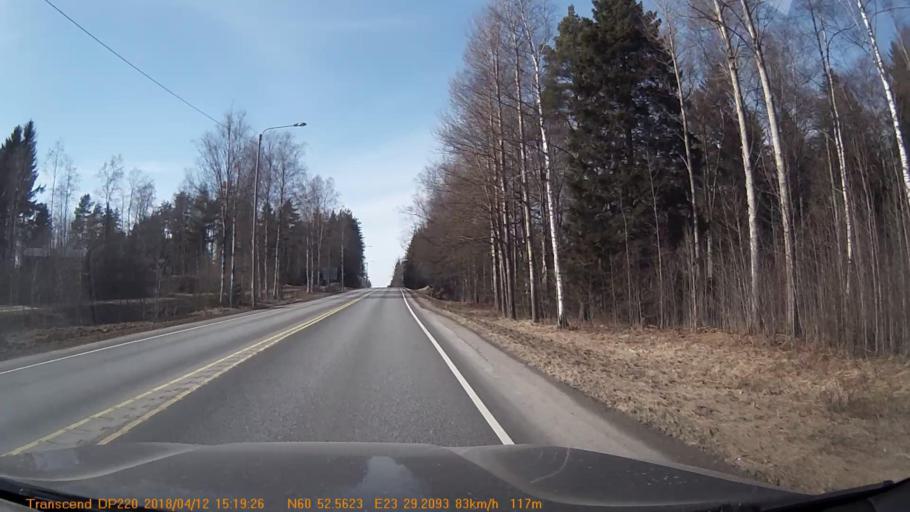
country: FI
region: Haeme
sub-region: Forssa
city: Jokioinen
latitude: 60.8763
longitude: 23.4863
